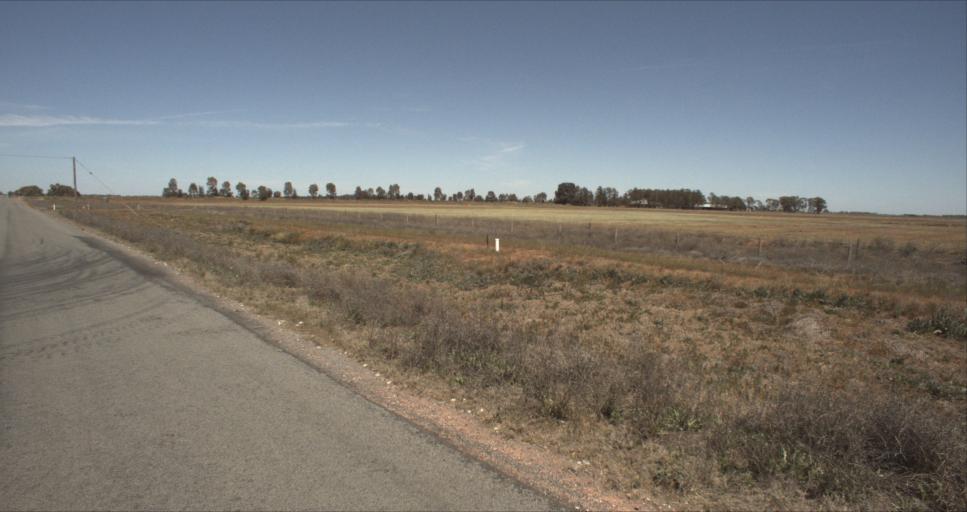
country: AU
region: New South Wales
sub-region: Leeton
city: Leeton
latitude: -34.4377
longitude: 146.2984
